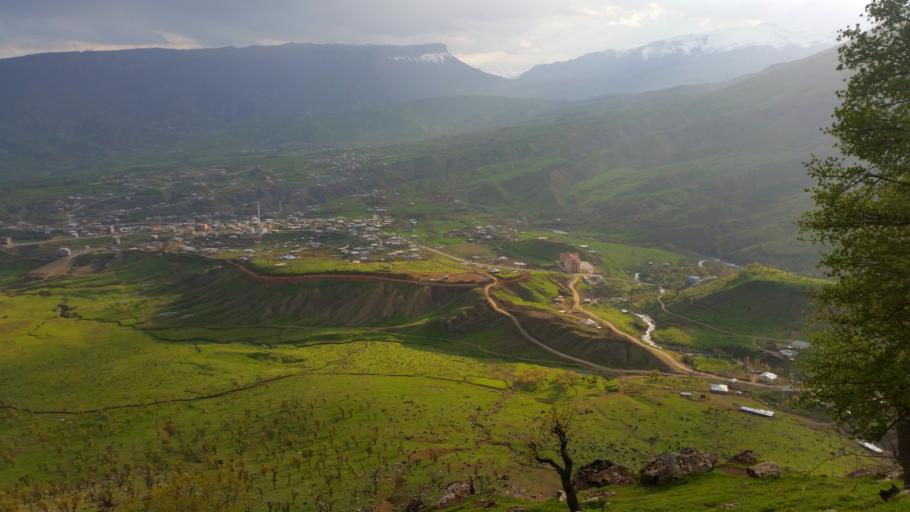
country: IQ
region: Arbil
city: Mergasur
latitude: 37.0977
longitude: 44.3222
